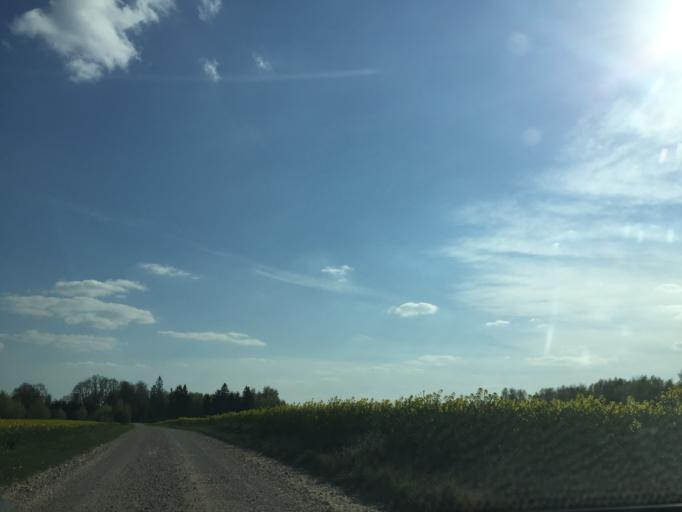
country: LV
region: Bauskas Rajons
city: Bauska
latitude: 56.4940
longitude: 24.3168
